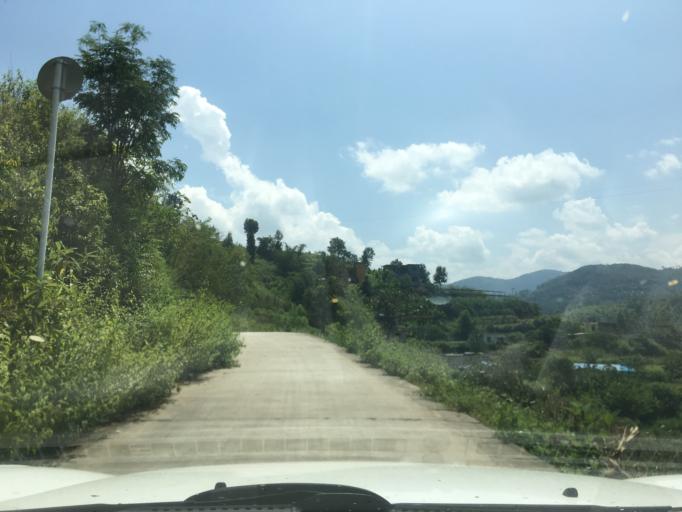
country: CN
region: Guangxi Zhuangzu Zizhiqu
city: Xinzhou
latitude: 25.4600
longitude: 105.7726
